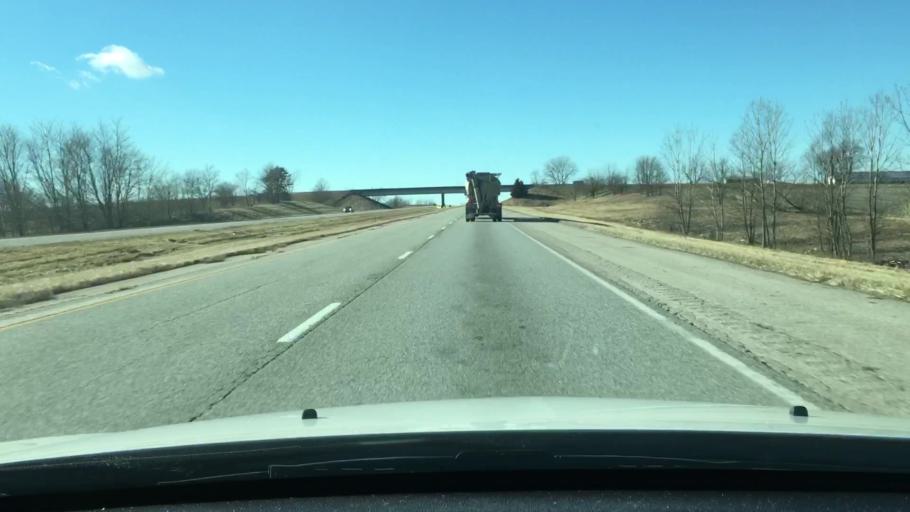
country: US
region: Illinois
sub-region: Pike County
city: Griggsville
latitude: 39.6784
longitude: -90.6999
